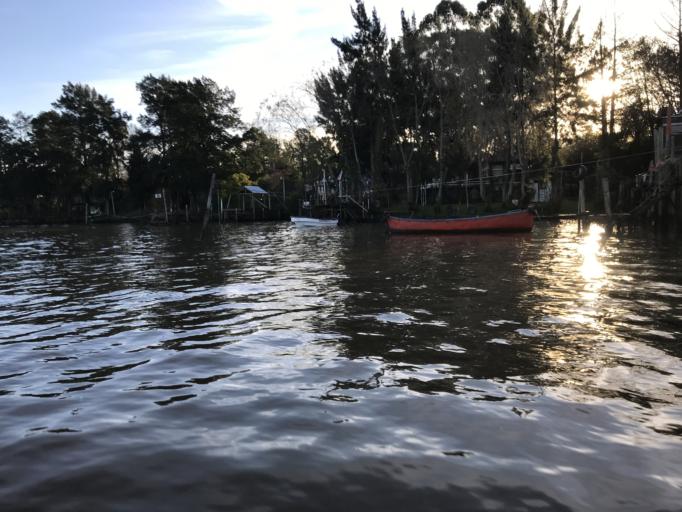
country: AR
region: Buenos Aires
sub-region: Partido de Tigre
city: Tigre
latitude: -34.3811
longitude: -58.5745
